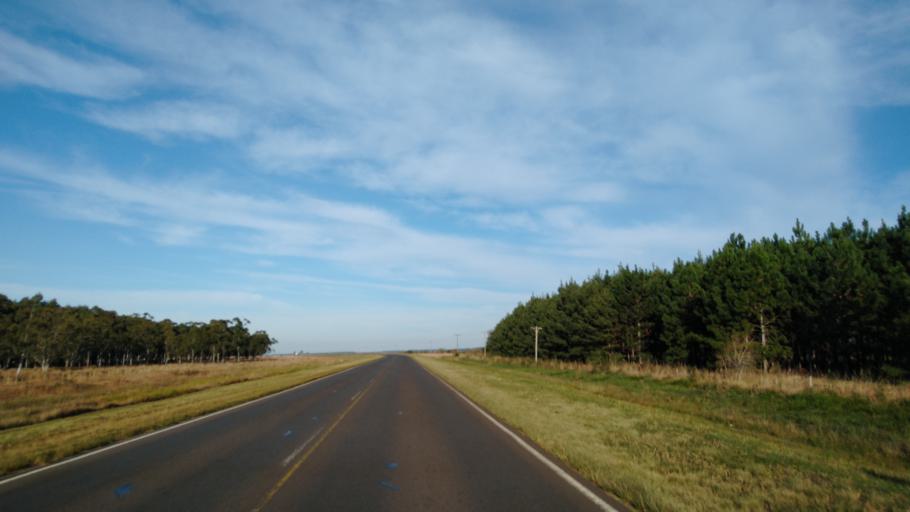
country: AR
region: Corrientes
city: La Cruz
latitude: -29.2537
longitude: -56.7430
